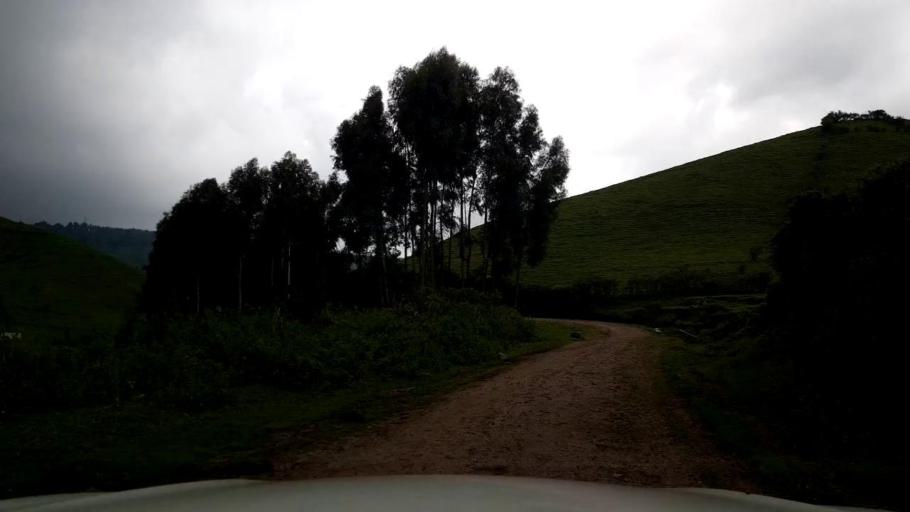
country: RW
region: Western Province
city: Gisenyi
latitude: -1.6865
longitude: 29.4191
